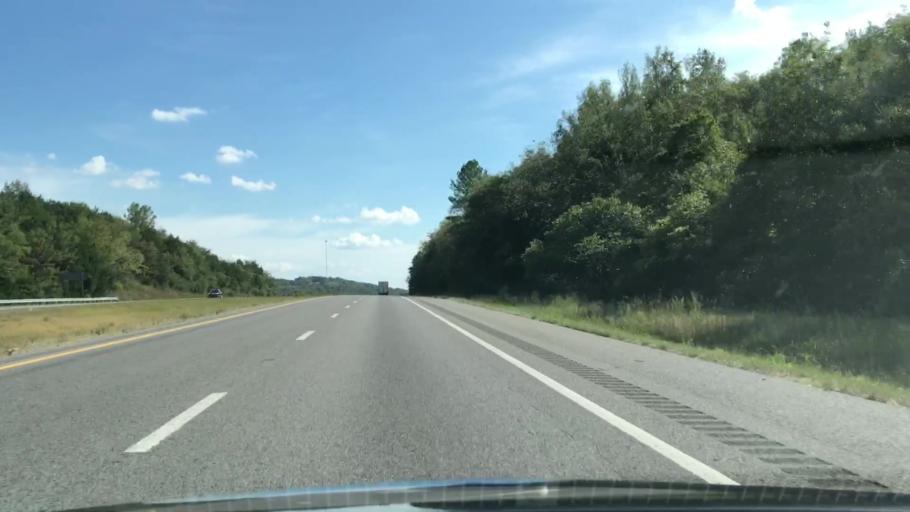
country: US
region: Alabama
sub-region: Limestone County
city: Ardmore
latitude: 35.0445
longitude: -86.8800
